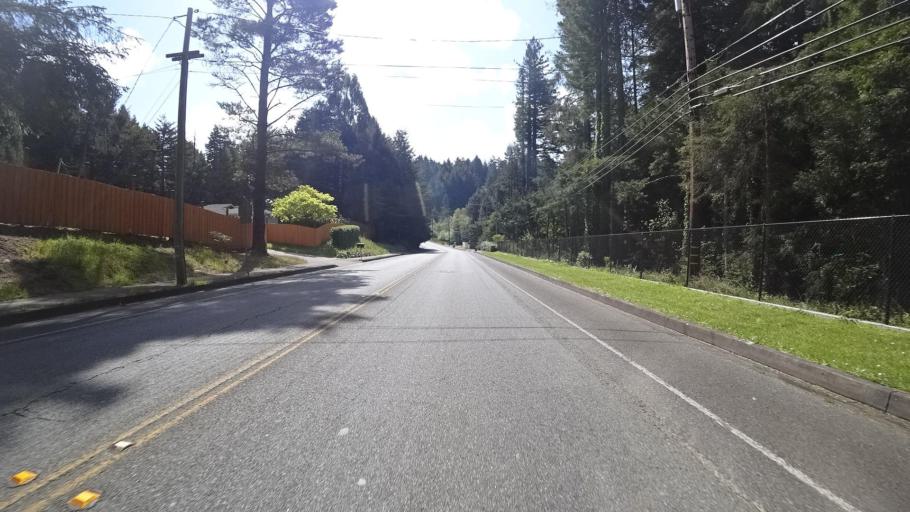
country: US
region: California
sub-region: Humboldt County
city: Cutten
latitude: 40.7693
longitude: -124.1596
